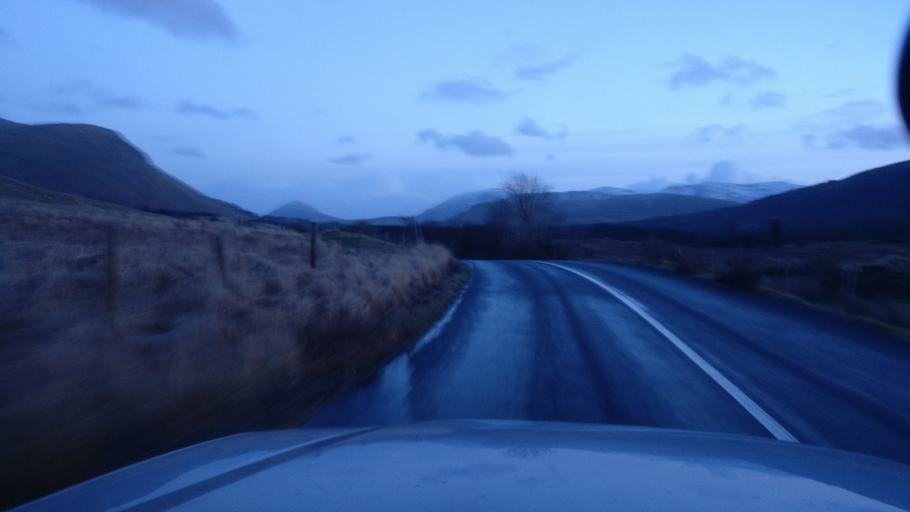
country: IE
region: Connaught
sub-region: Maigh Eo
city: Westport
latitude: 53.5573
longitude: -9.6443
